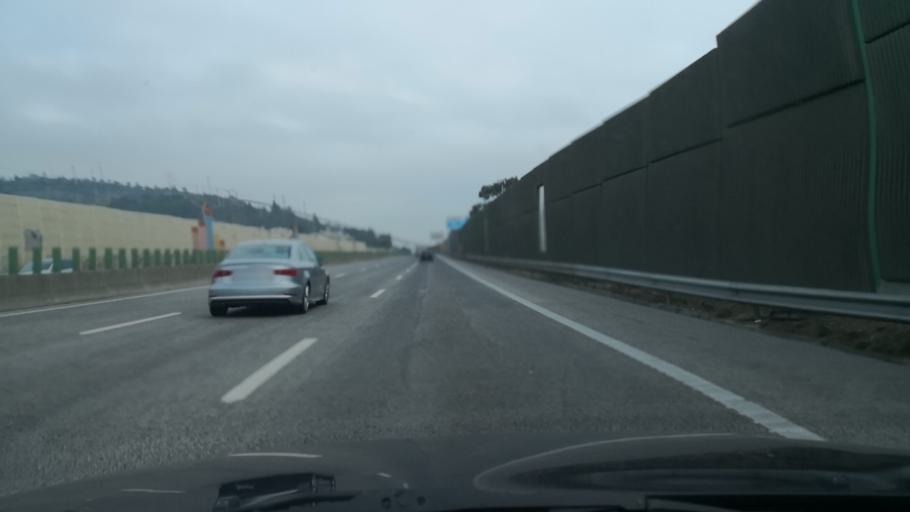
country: PT
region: Lisbon
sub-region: Vila Franca de Xira
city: Sobralinho
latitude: 38.9142
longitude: -9.0261
